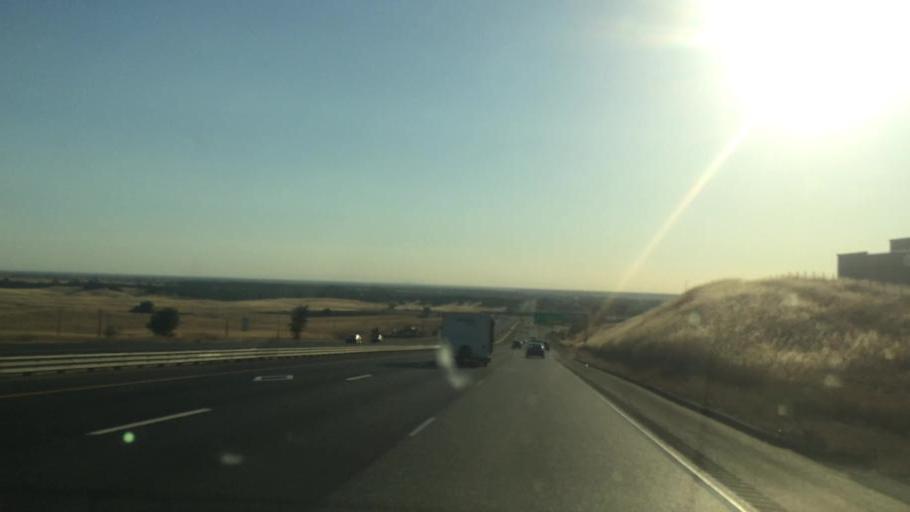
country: US
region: California
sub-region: El Dorado County
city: El Dorado Hills
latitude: 38.6441
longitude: -121.1027
